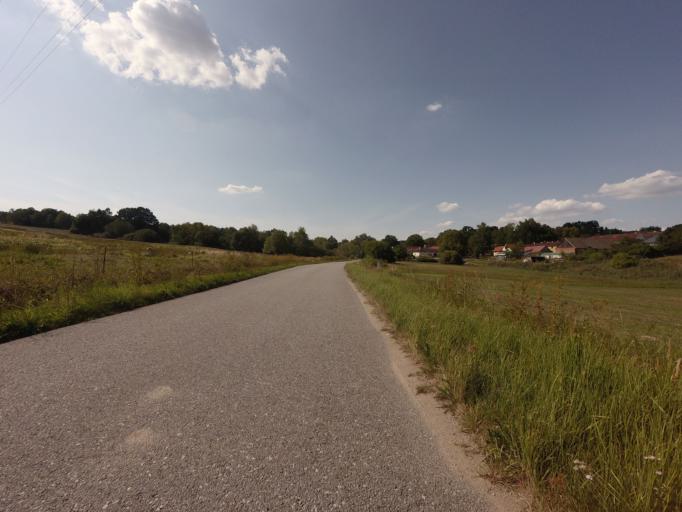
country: CZ
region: Jihocesky
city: Tyn nad Vltavou
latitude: 49.1717
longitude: 14.4213
